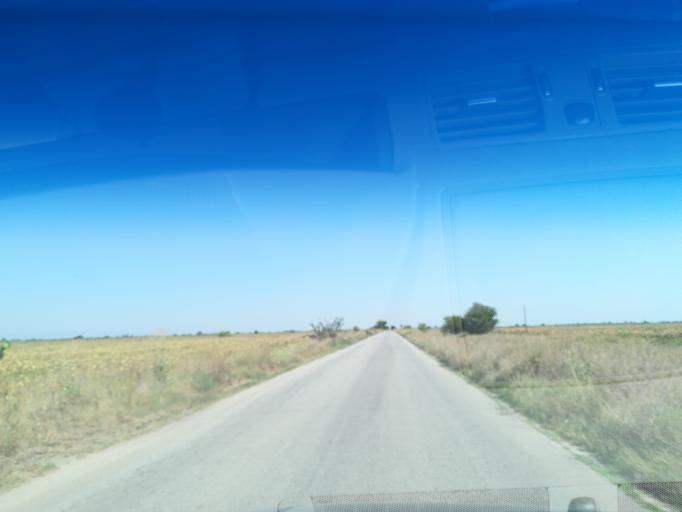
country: BG
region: Plovdiv
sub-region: Obshtina Suedinenie
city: Suedinenie
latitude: 42.2517
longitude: 24.4563
